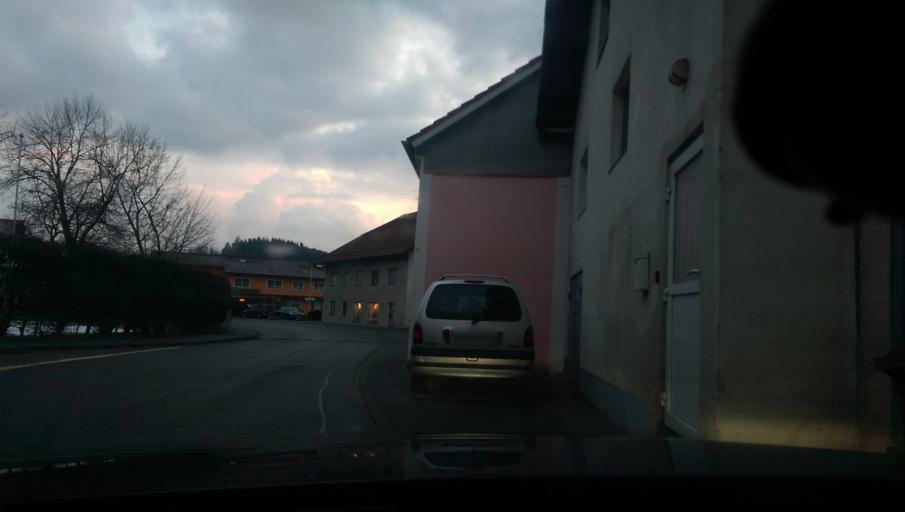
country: DE
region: Bavaria
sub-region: Lower Bavaria
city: Haselbach
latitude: 48.6465
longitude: 13.3881
